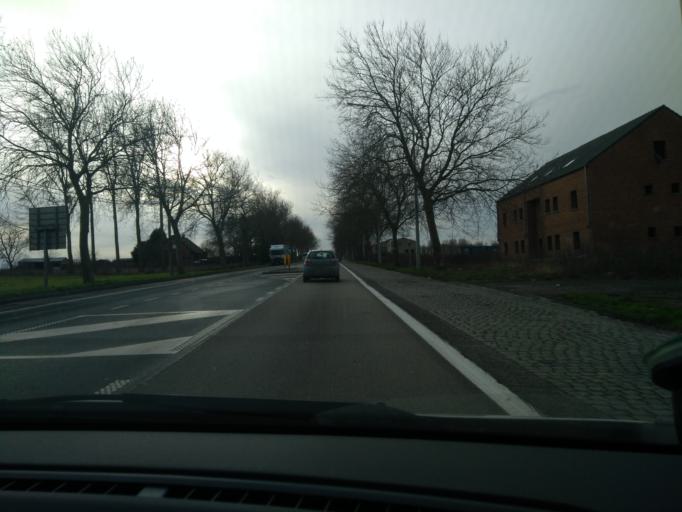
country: BE
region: Wallonia
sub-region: Province du Hainaut
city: Quevy-le-Petit
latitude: 50.3489
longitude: 3.9687
